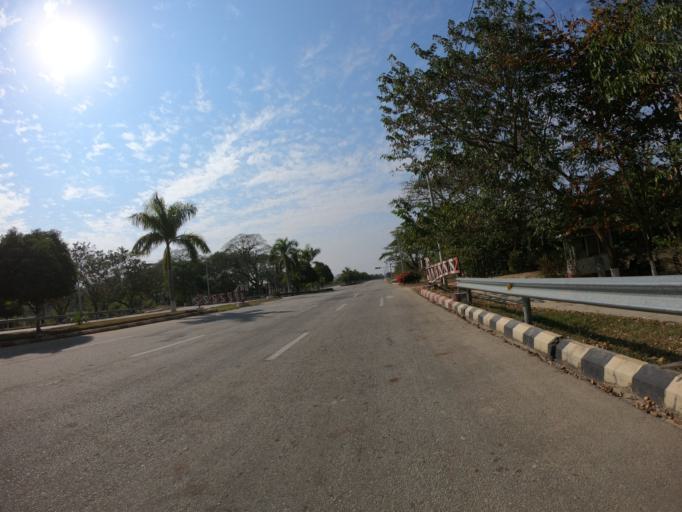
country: MM
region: Mandalay
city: Nay Pyi Taw
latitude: 19.6529
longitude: 96.1393
